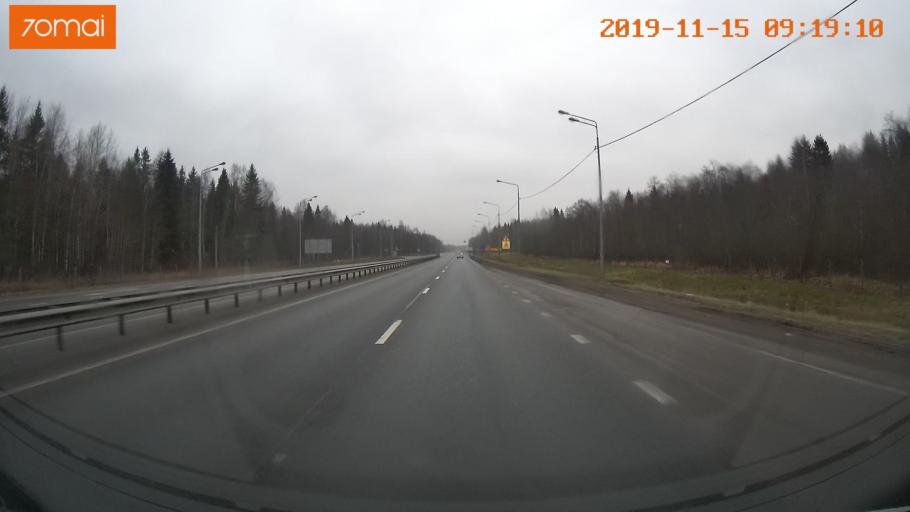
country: RU
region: Vologda
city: Tonshalovo
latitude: 59.2815
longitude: 38.0111
